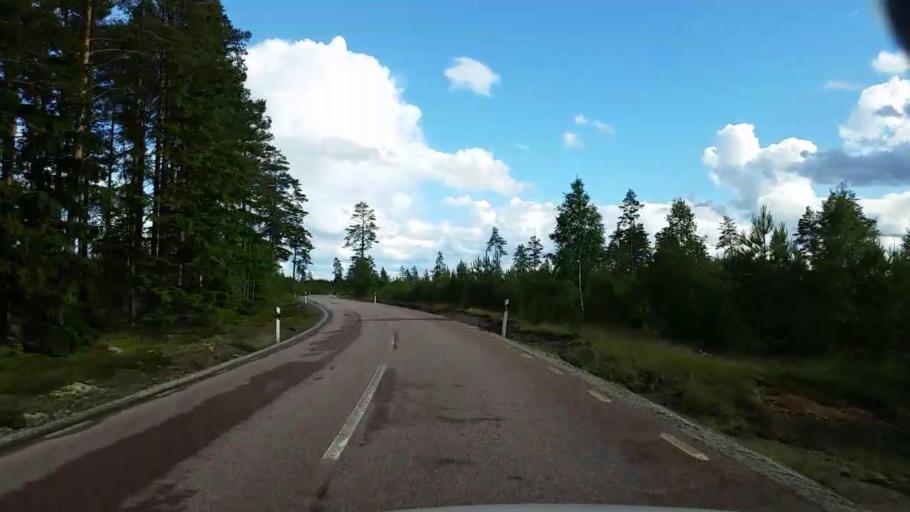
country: SE
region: Vaestmanland
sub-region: Fagersta Kommun
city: Fagersta
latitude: 59.8949
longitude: 15.8209
